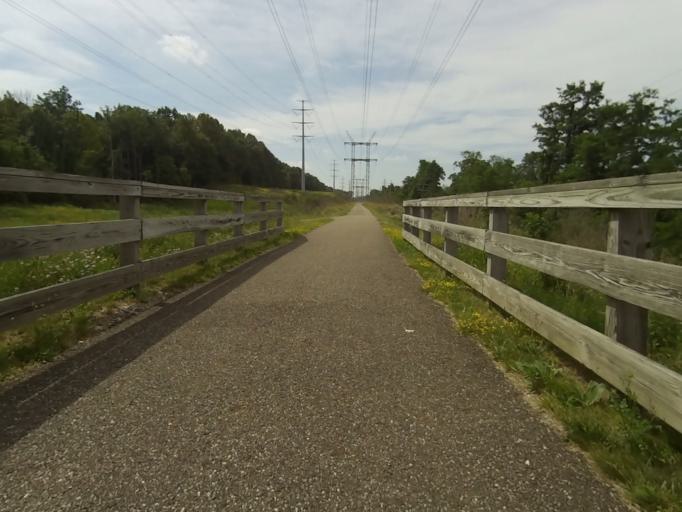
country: US
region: Ohio
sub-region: Cuyahoga County
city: Walton Hills
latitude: 41.3389
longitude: -81.5711
